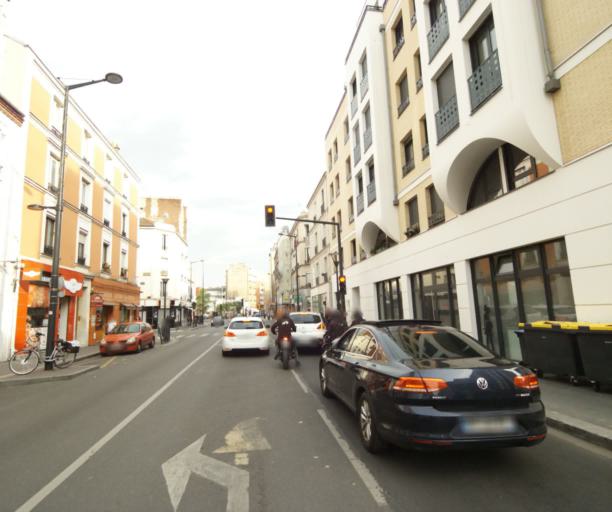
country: FR
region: Ile-de-France
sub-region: Paris
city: Saint-Ouen
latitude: 48.8932
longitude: 2.3354
